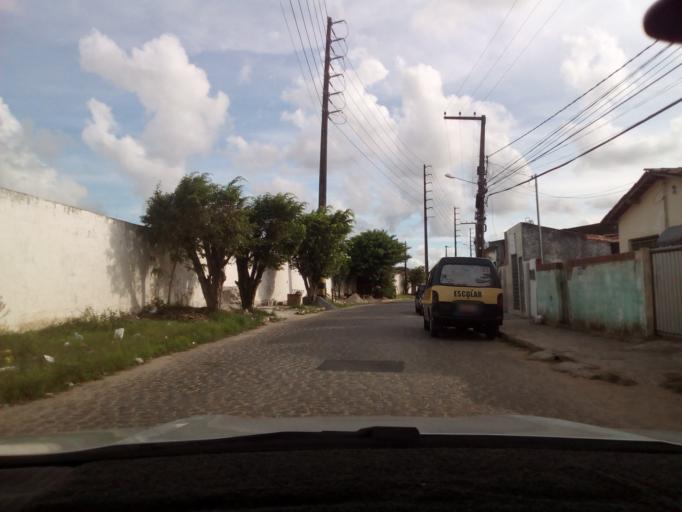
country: BR
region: Paraiba
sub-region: Joao Pessoa
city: Joao Pessoa
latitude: -7.1661
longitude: -34.8813
